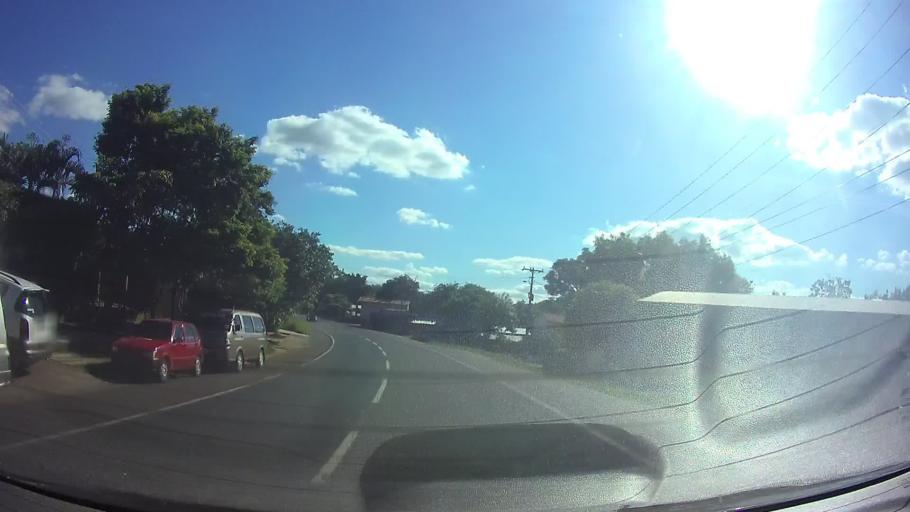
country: PY
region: Cordillera
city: Caacupe
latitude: -25.3852
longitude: -57.1322
